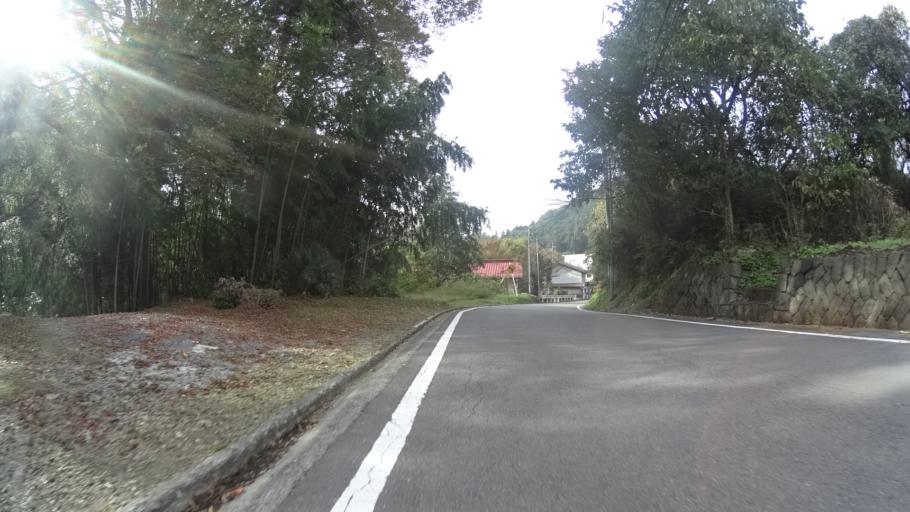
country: JP
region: Yamanashi
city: Otsuki
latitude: 35.6145
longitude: 139.0153
